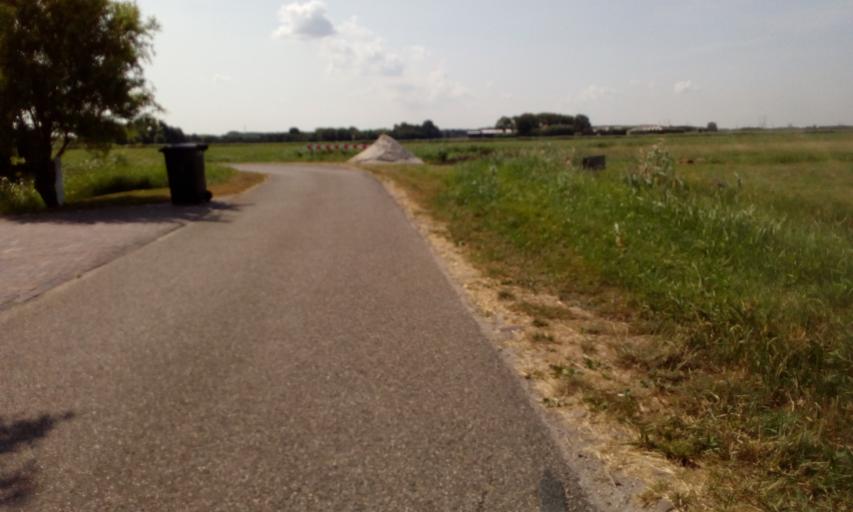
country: NL
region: South Holland
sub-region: Gemeente Vlaardingen
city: Vlaardingen
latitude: 51.9547
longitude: 4.3139
